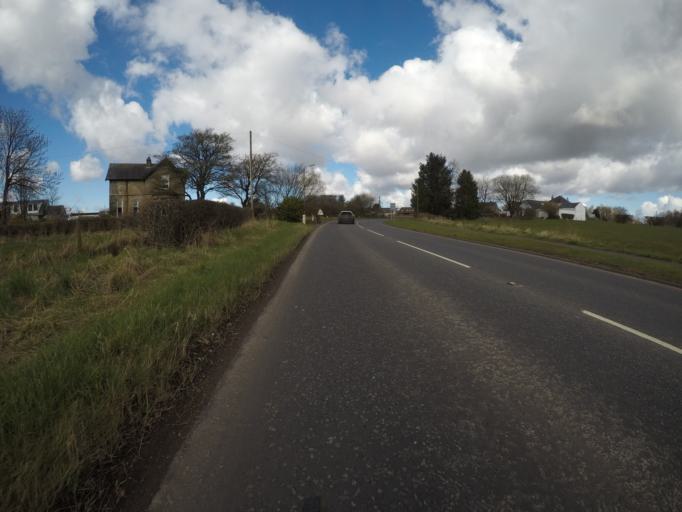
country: GB
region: Scotland
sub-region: North Ayrshire
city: Beith
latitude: 55.7451
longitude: -4.6285
